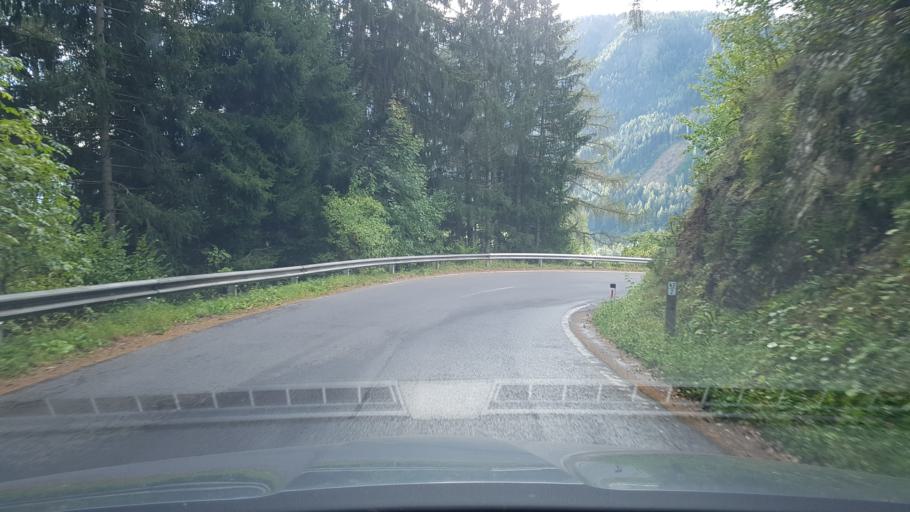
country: AT
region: Styria
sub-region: Politischer Bezirk Murau
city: Schoder
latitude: 47.1912
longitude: 14.1255
